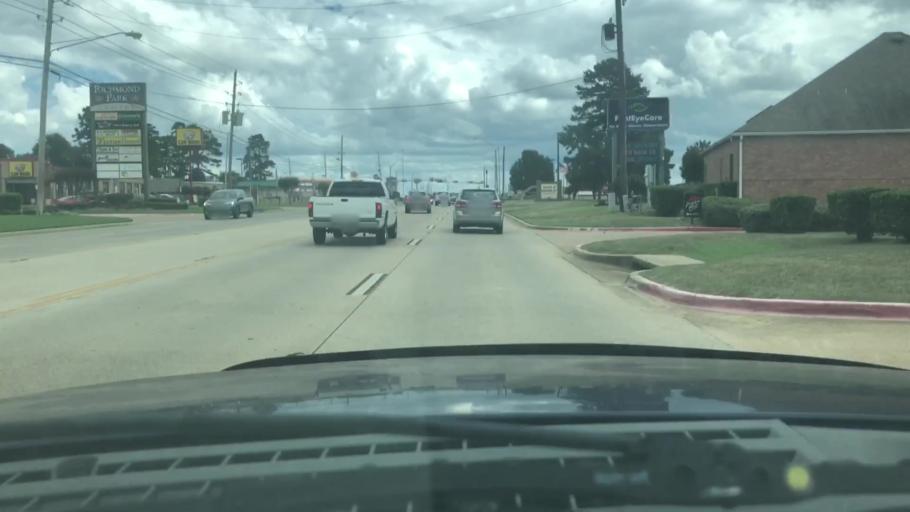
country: US
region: Texas
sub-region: Bowie County
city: Wake Village
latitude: 33.4620
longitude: -94.0923
